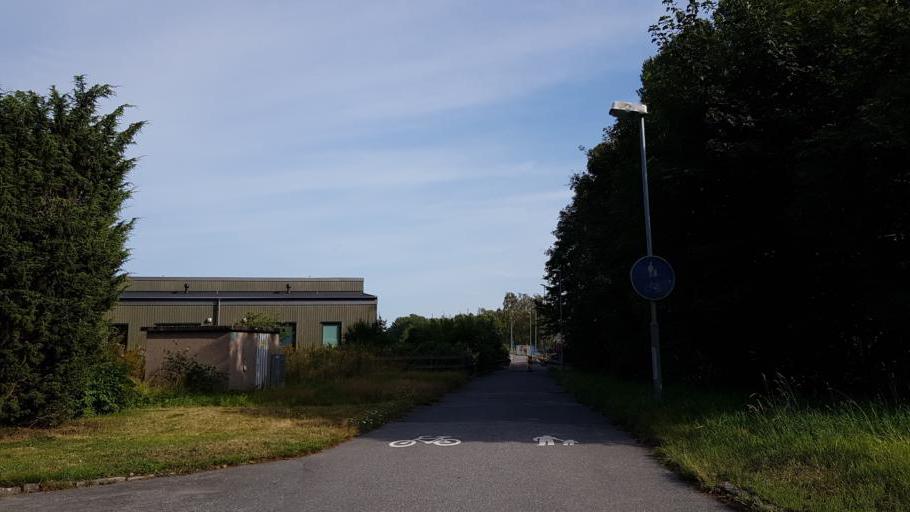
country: SE
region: Vaestra Goetaland
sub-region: Molndal
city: Moelndal
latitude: 57.6664
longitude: 12.0349
